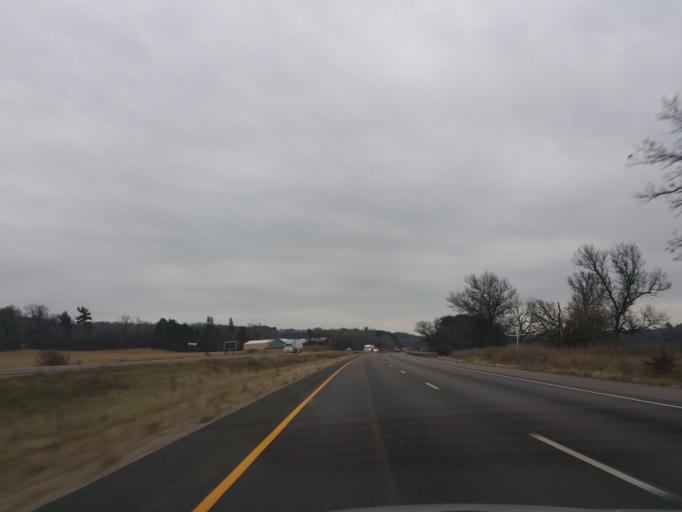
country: US
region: Wisconsin
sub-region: Eau Claire County
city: Fall Creek
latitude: 44.7245
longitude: -91.3566
